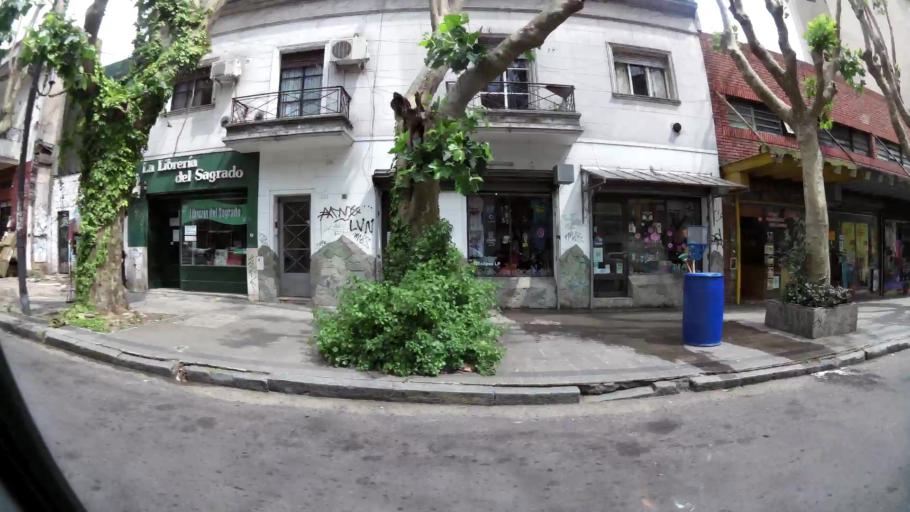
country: AR
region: Buenos Aires
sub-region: Partido de La Plata
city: La Plata
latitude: -34.9215
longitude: -57.9515
